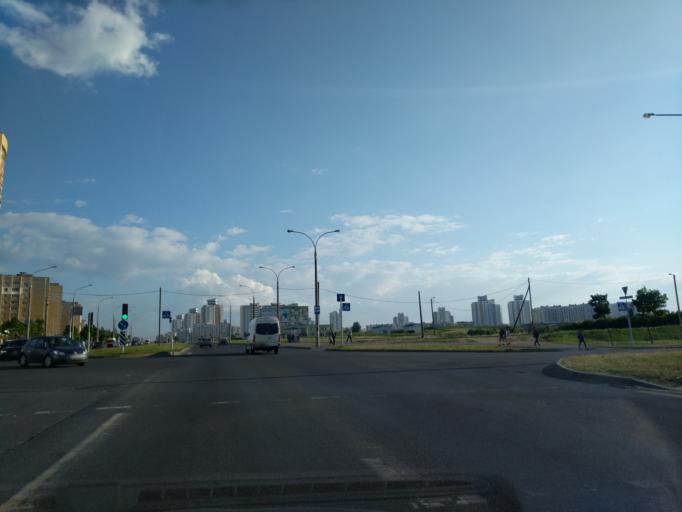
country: BY
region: Minsk
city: Zhdanovichy
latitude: 53.9211
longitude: 27.4380
